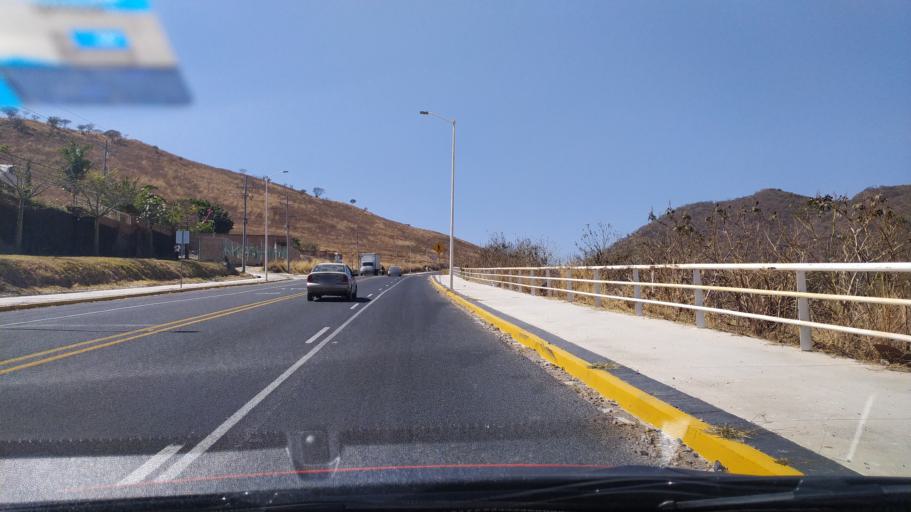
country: MX
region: Jalisco
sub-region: Tlajomulco de Zuniga
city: Lomas del Sur
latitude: 20.4893
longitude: -103.4199
